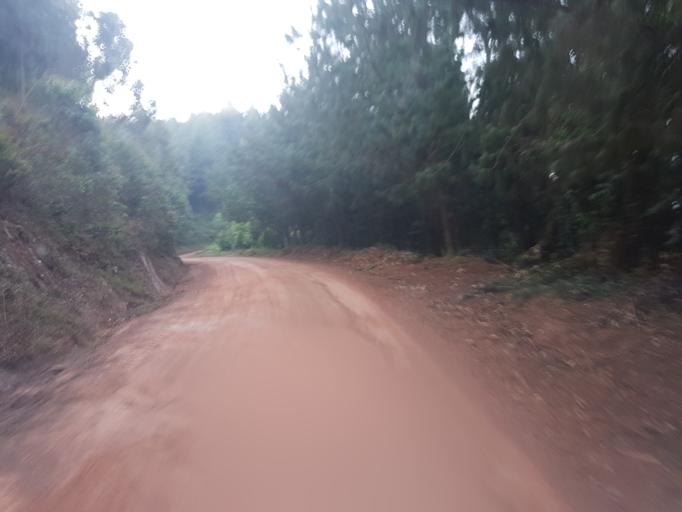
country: UG
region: Western Region
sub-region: Kanungu District
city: Kanungu
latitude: -1.0458
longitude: 29.8831
